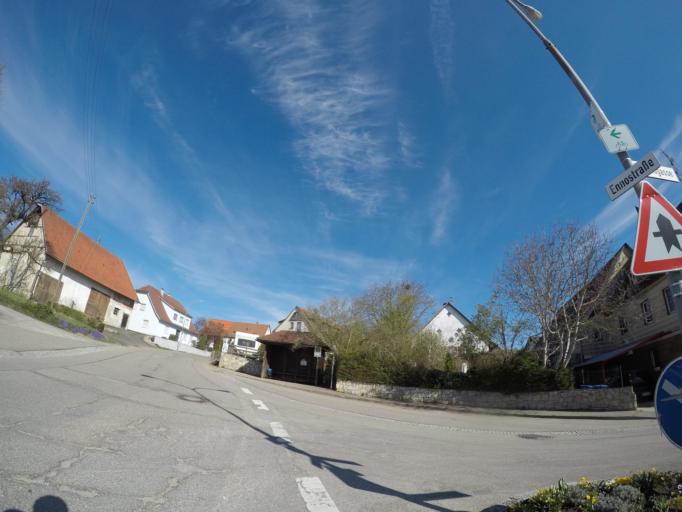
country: DE
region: Baden-Wuerttemberg
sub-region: Tuebingen Region
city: Allmendingen
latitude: 48.3498
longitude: 9.6606
